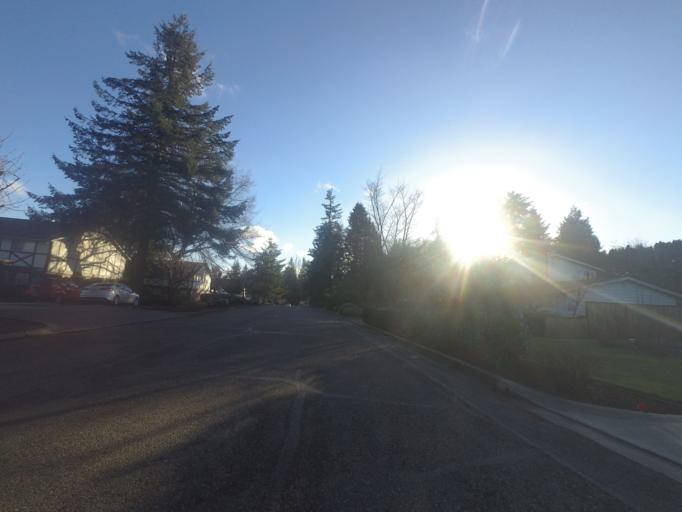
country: US
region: Washington
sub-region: Pierce County
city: Fircrest
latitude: 47.2228
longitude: -122.5192
